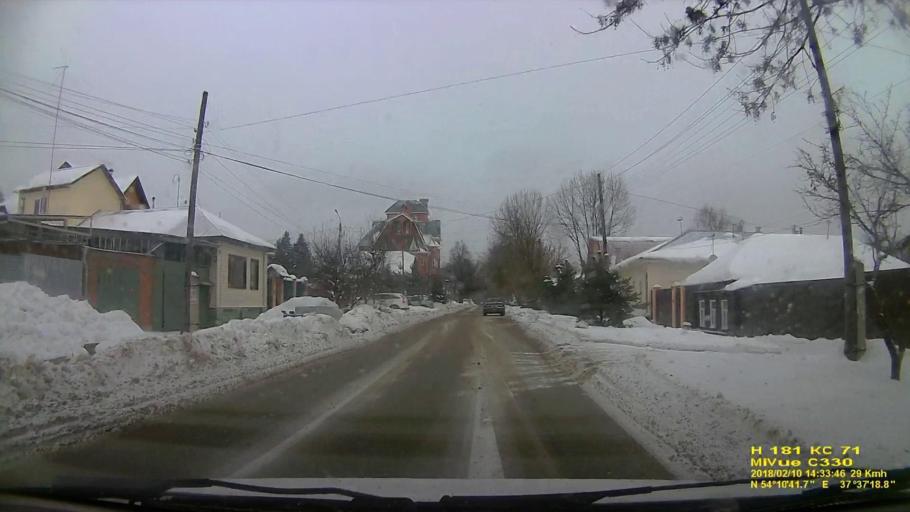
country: RU
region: Tula
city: Tula
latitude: 54.1783
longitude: 37.6218
